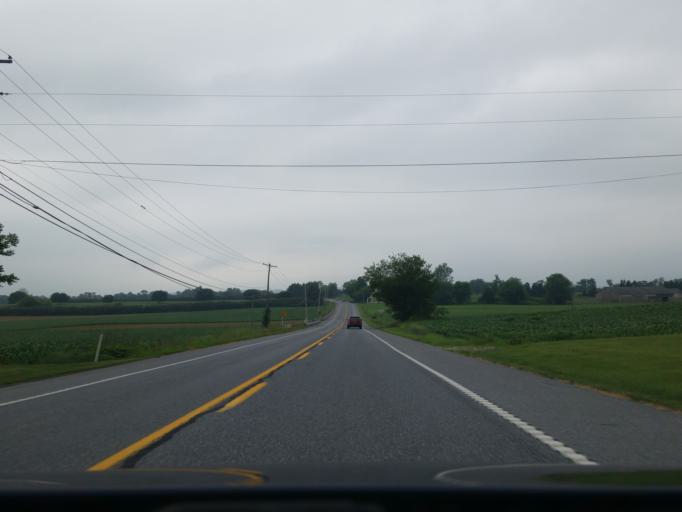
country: US
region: Pennsylvania
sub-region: Lebanon County
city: Annville
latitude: 40.2983
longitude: -76.4926
